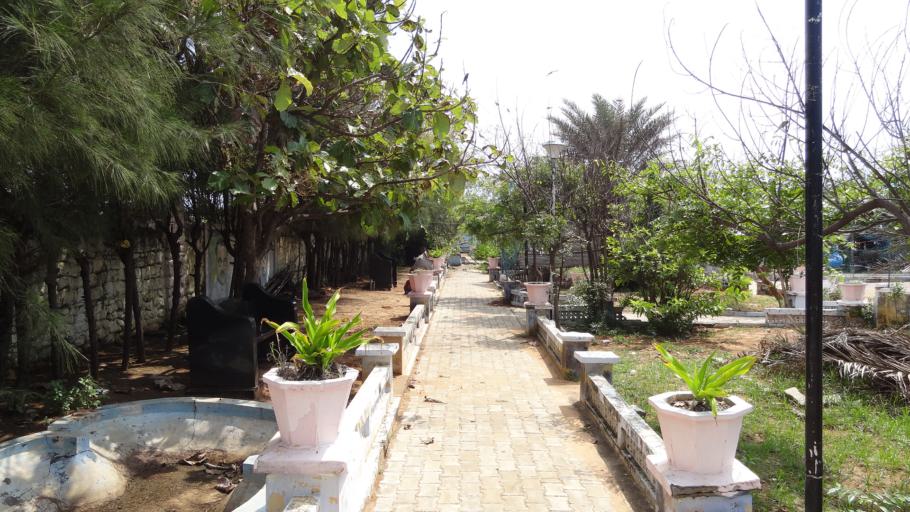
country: IN
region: Tamil Nadu
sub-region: Kanniyakumari
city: Kanniyakumari
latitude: 8.0794
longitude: 77.5483
